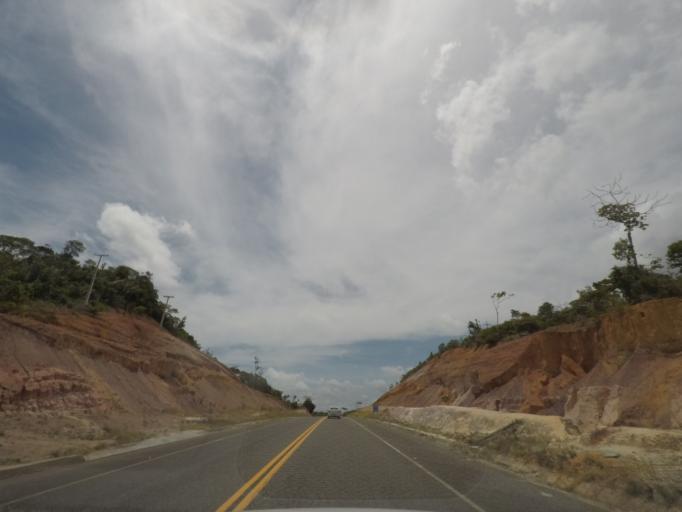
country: BR
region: Bahia
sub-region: Conde
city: Conde
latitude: -11.9181
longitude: -37.6631
